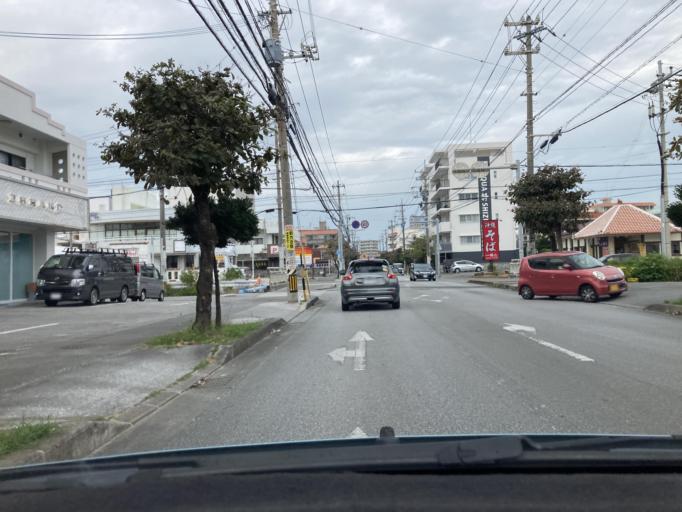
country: JP
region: Okinawa
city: Chatan
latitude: 26.3063
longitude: 127.7607
